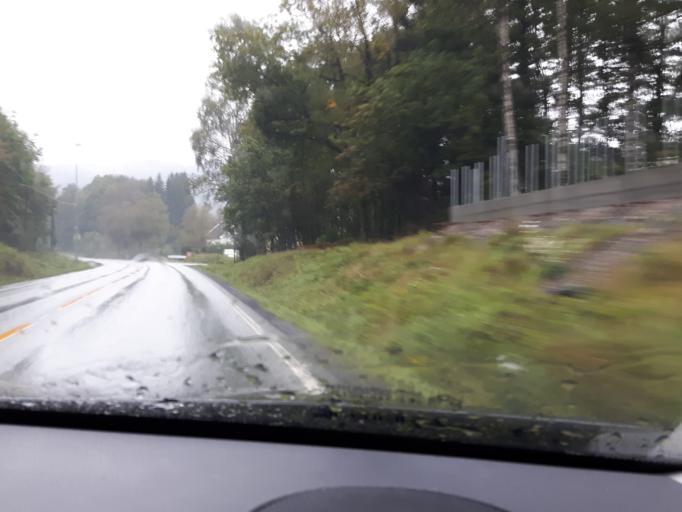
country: NO
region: Vest-Agder
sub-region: Lindesnes
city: Vigeland
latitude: 58.0693
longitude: 7.3494
